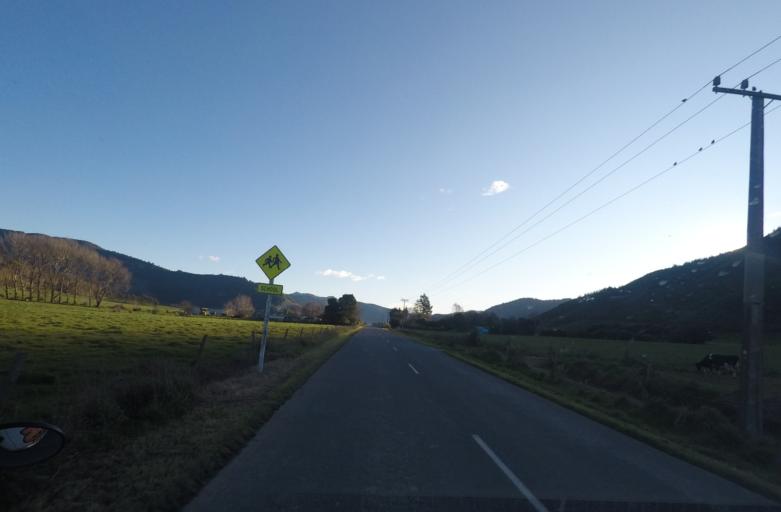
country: NZ
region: Marlborough
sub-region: Marlborough District
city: Picton
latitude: -41.2901
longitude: 173.8824
